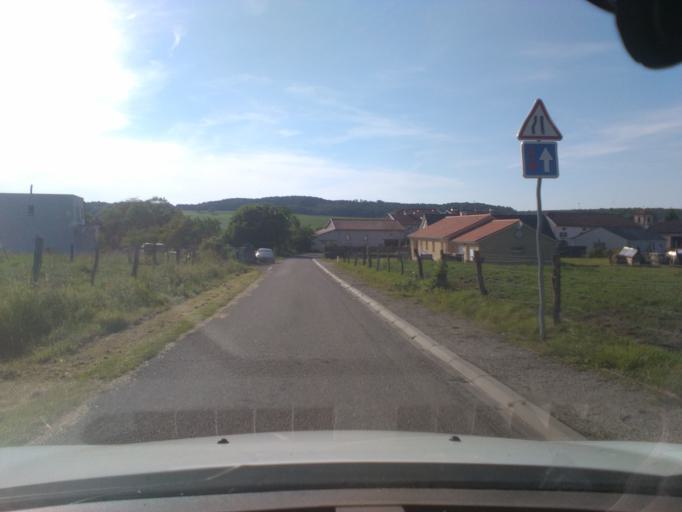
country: FR
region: Lorraine
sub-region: Departement des Vosges
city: Mirecourt
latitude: 48.2642
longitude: 6.2284
